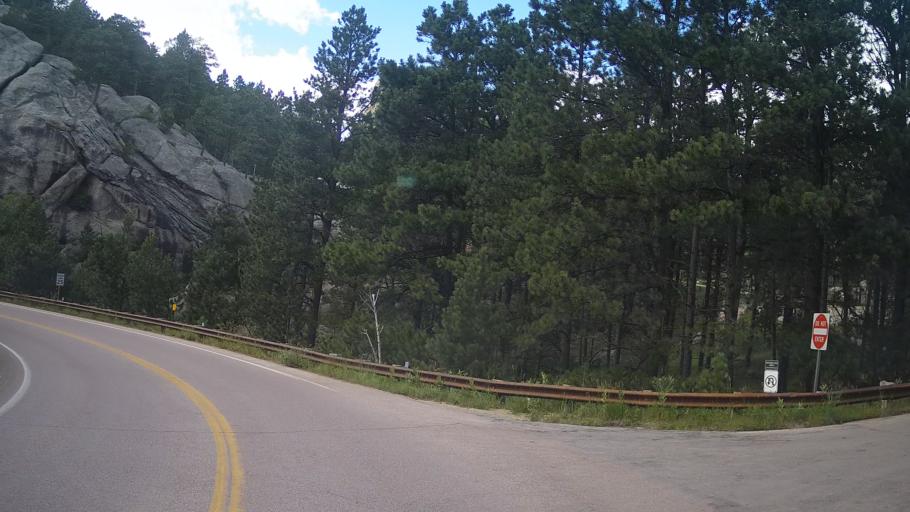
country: US
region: South Dakota
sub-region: Custer County
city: Custer
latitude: 43.8749
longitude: -103.4559
